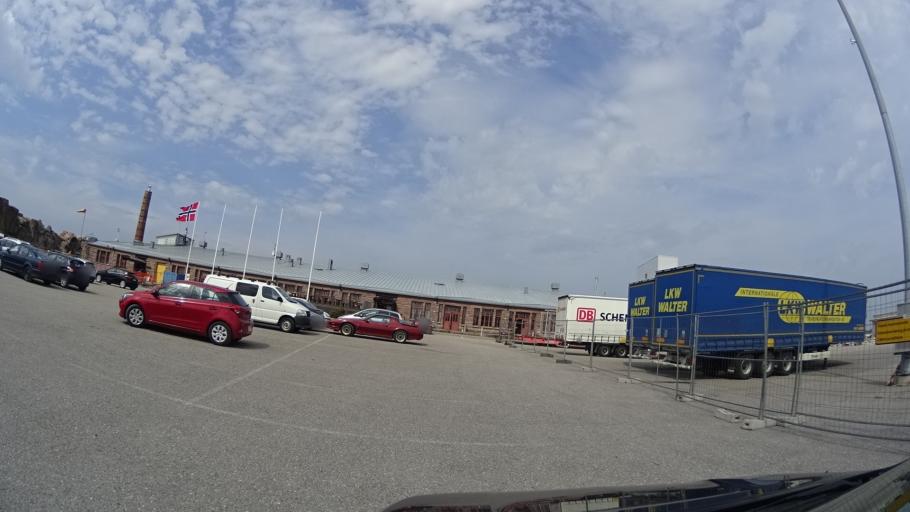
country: FI
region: Uusimaa
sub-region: Raaseporin
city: Hanko
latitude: 59.8191
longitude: 22.9467
